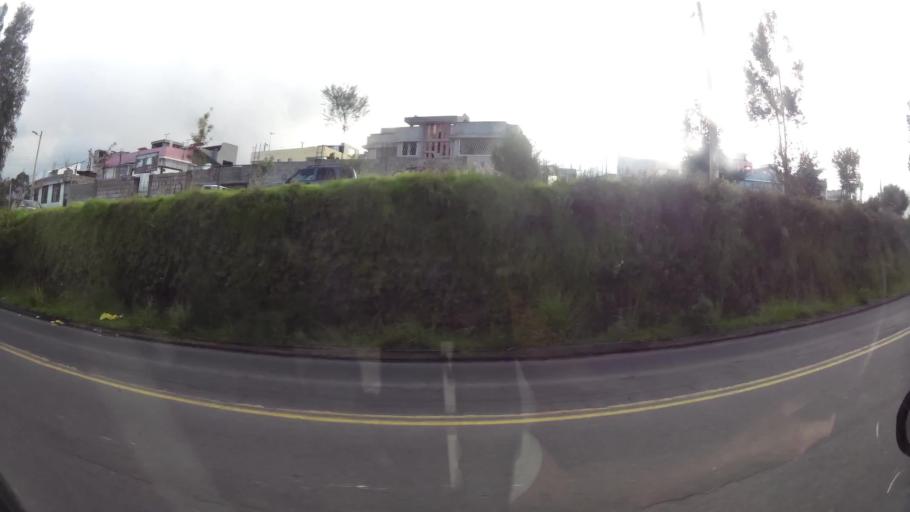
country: EC
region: Pichincha
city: Quito
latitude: -0.2577
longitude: -78.4939
